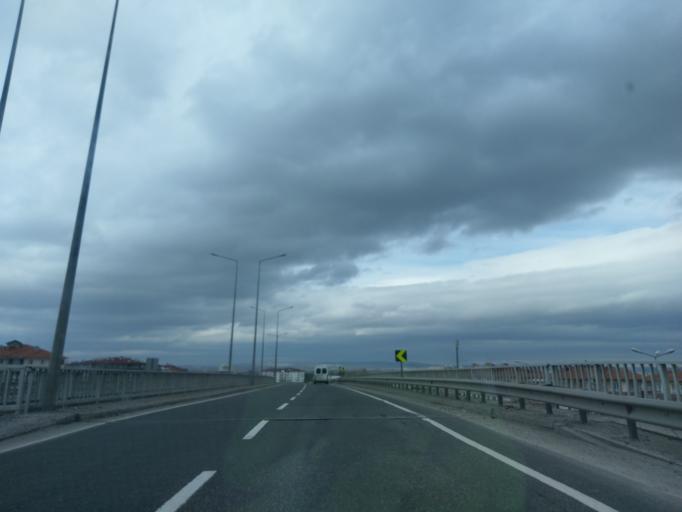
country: TR
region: Kuetahya
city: Kutahya
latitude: 39.4050
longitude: 30.0289
